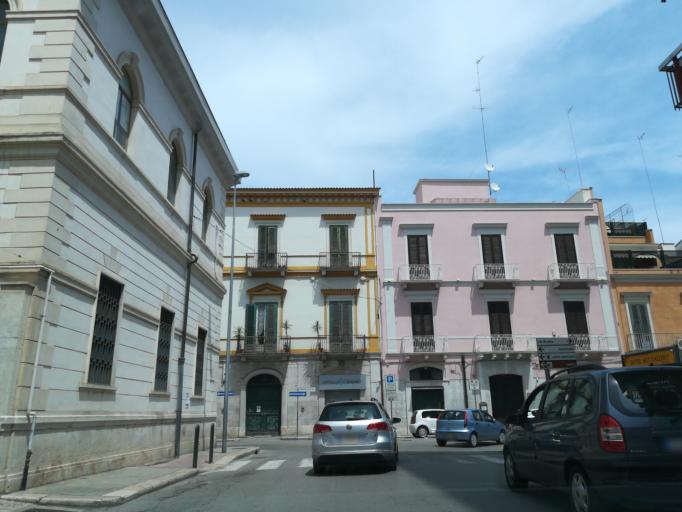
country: IT
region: Apulia
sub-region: Provincia di Barletta - Andria - Trani
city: Barletta
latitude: 41.3179
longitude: 16.2813
